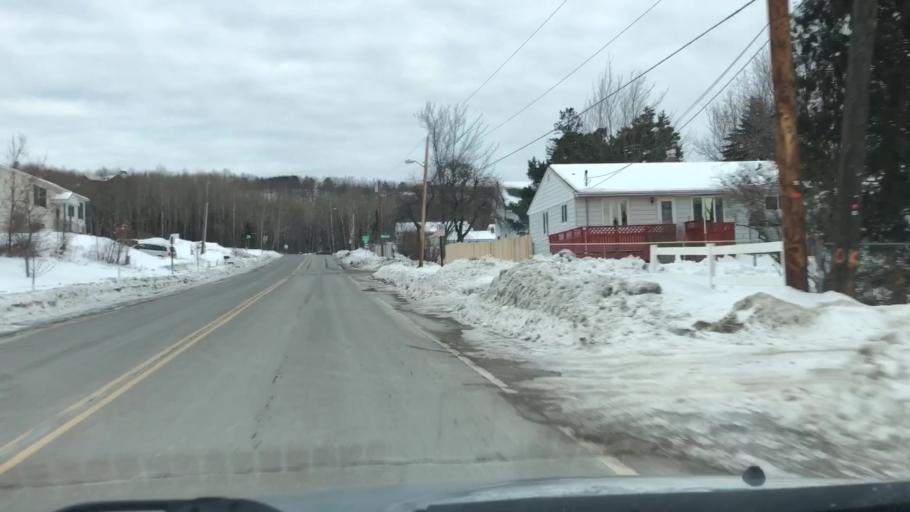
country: US
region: Minnesota
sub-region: Saint Louis County
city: Arnold
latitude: 46.8388
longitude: -92.0371
